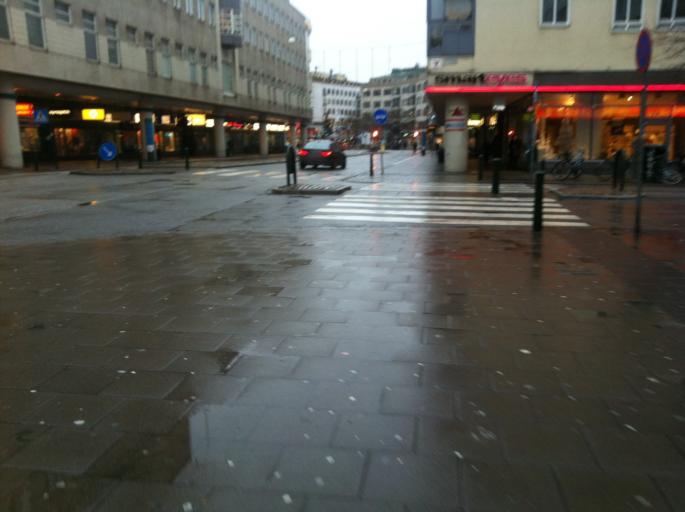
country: SE
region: Skane
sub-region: Malmo
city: Malmoe
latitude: 55.5958
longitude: 13.0030
